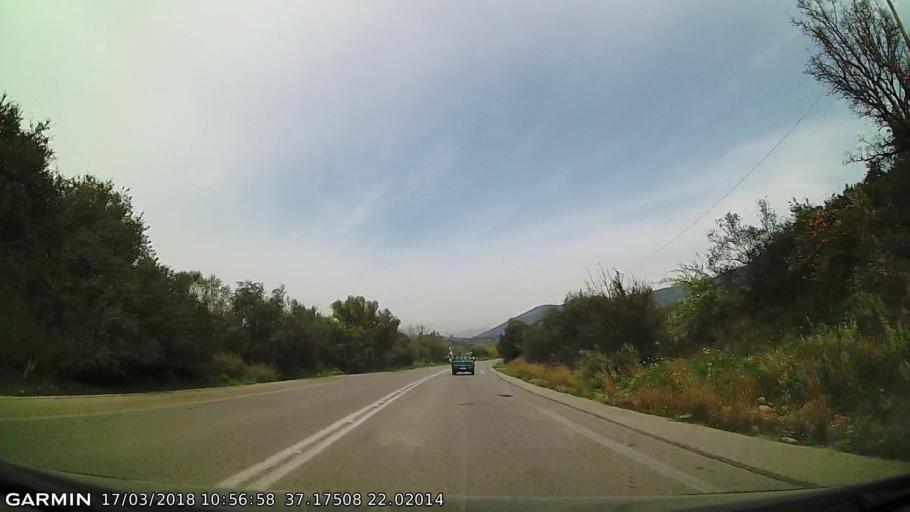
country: GR
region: Peloponnese
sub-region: Nomos Messinias
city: Arfara
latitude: 37.1753
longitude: 22.0200
